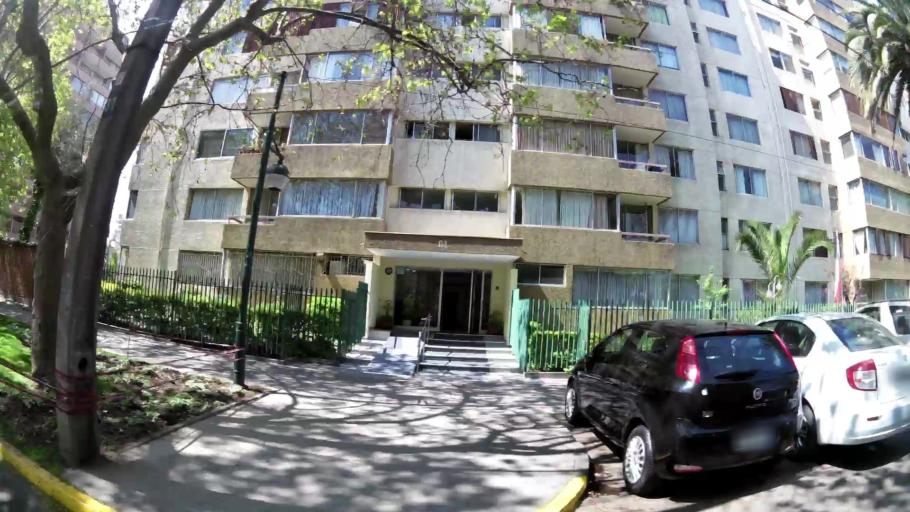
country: CL
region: Santiago Metropolitan
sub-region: Provincia de Santiago
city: Villa Presidente Frei, Nunoa, Santiago, Chile
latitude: -33.4537
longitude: -70.6034
